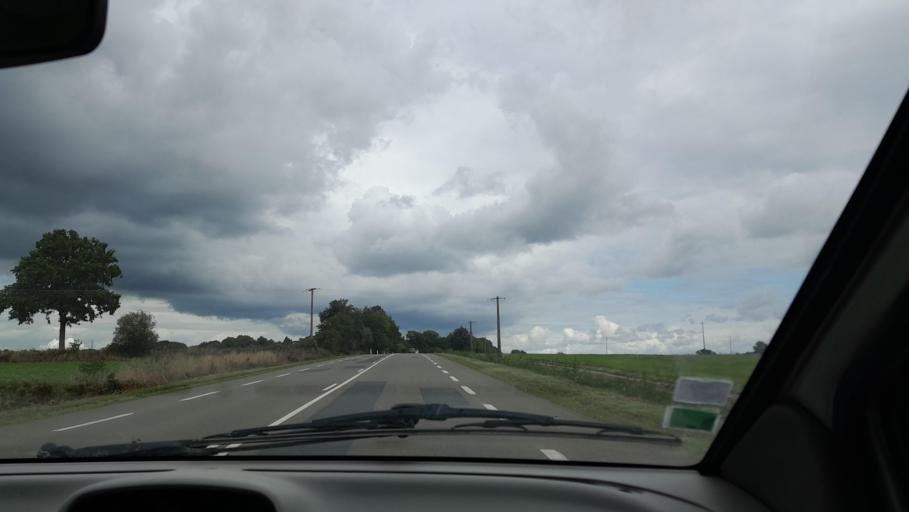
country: FR
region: Pays de la Loire
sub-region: Departement de la Mayenne
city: Ahuille
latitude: 47.9959
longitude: -0.8483
